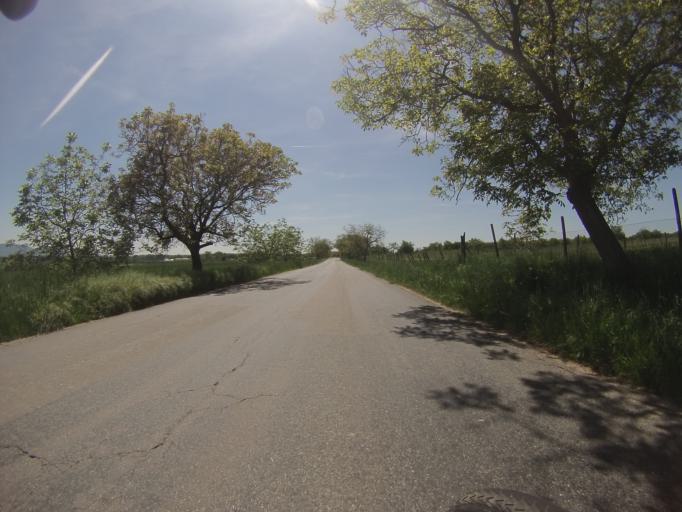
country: CZ
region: South Moravian
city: Vranovice
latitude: 48.9357
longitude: 16.5819
